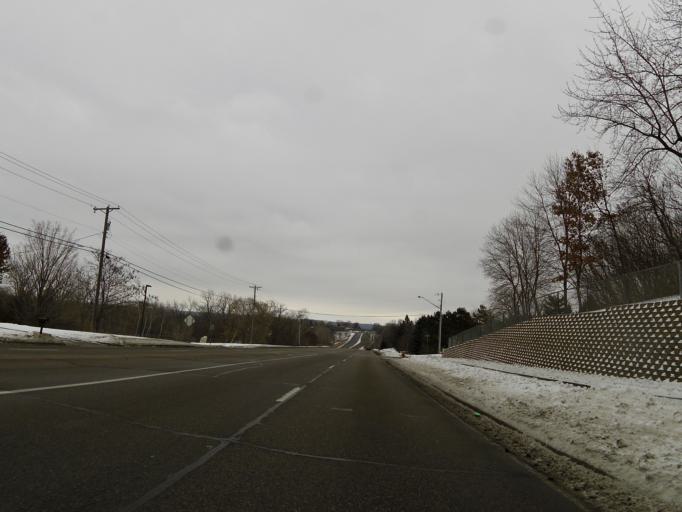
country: US
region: Minnesota
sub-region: Dakota County
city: Inver Grove Heights
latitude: 44.8479
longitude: -93.0524
